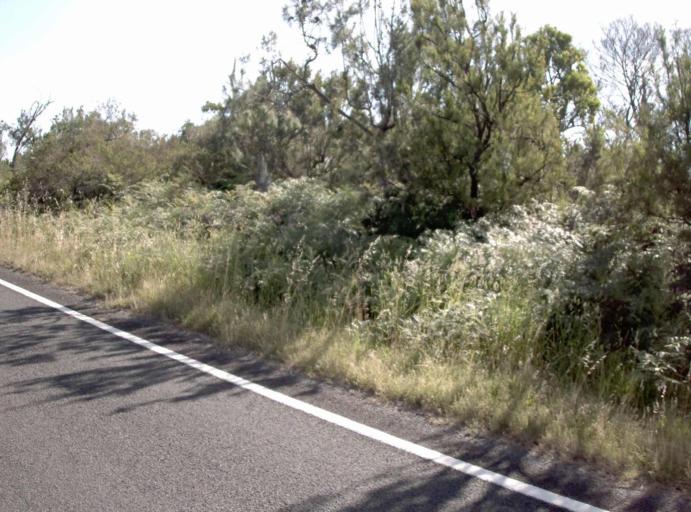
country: AU
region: Victoria
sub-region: Cardinia
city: Koo-Wee-Rup
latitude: -38.3026
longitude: 145.5433
